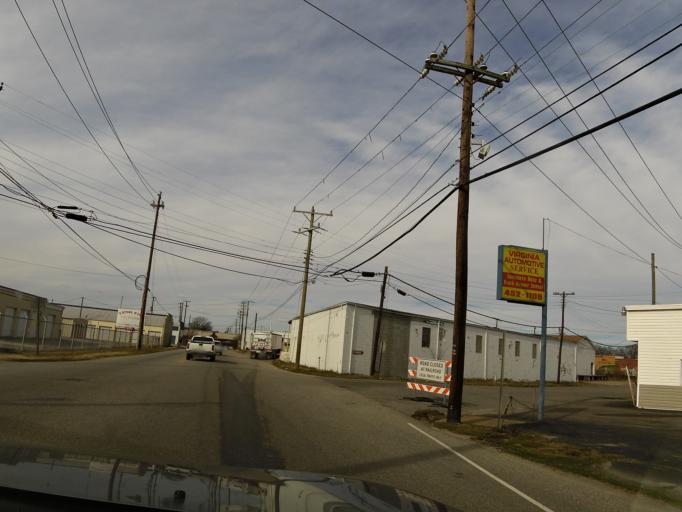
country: US
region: Virginia
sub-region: City of Hopewell
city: Hopewell
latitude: 37.3018
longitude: -77.2819
